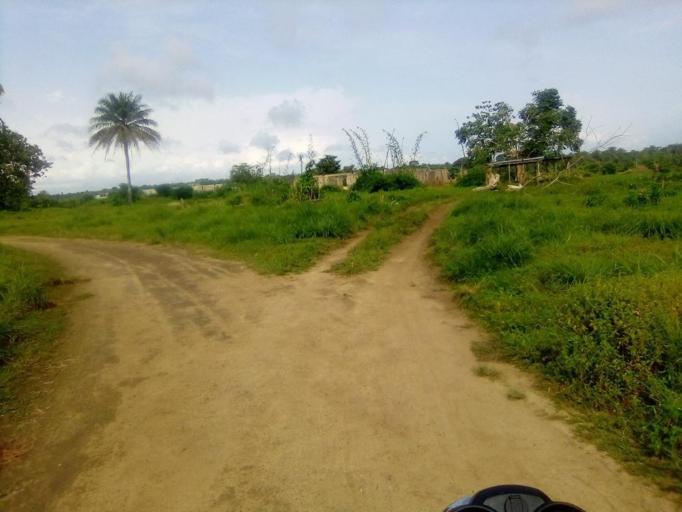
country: SL
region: Southern Province
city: Pujehun
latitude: 7.3621
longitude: -11.7298
